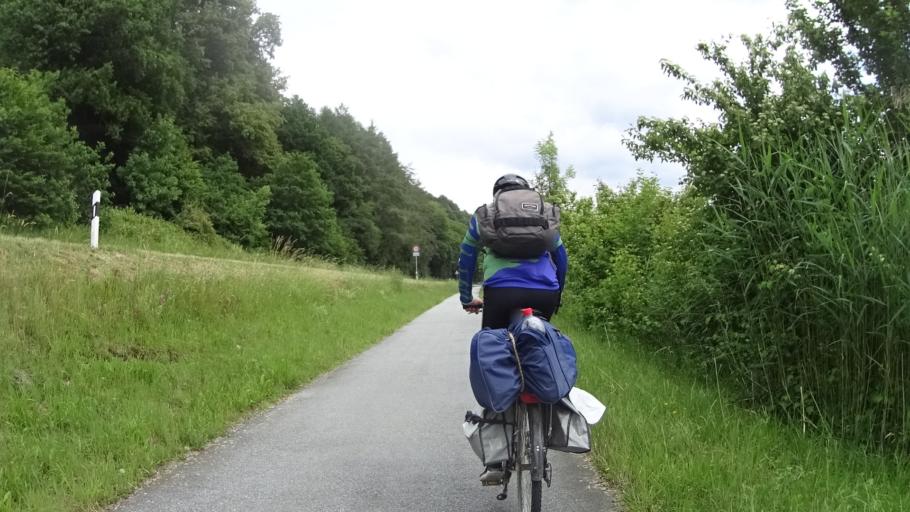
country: DE
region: Bavaria
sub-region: Lower Bavaria
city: Aicha vorm Wald
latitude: 48.6128
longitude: 13.2866
